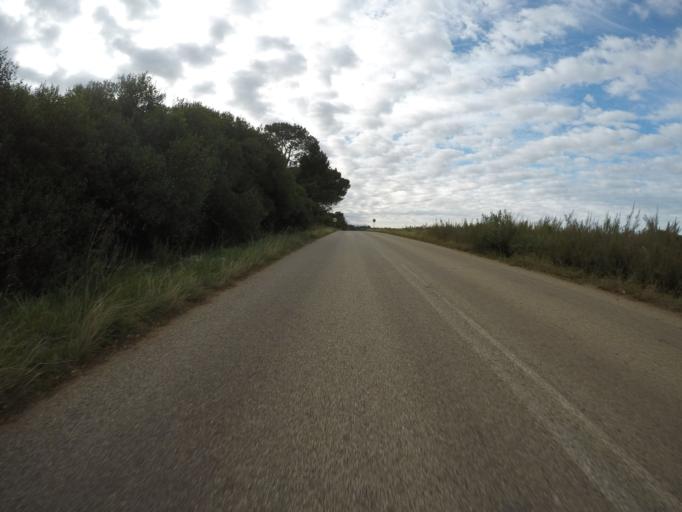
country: ZA
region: Eastern Cape
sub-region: Cacadu District Municipality
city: Kareedouw
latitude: -34.0057
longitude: 24.2414
